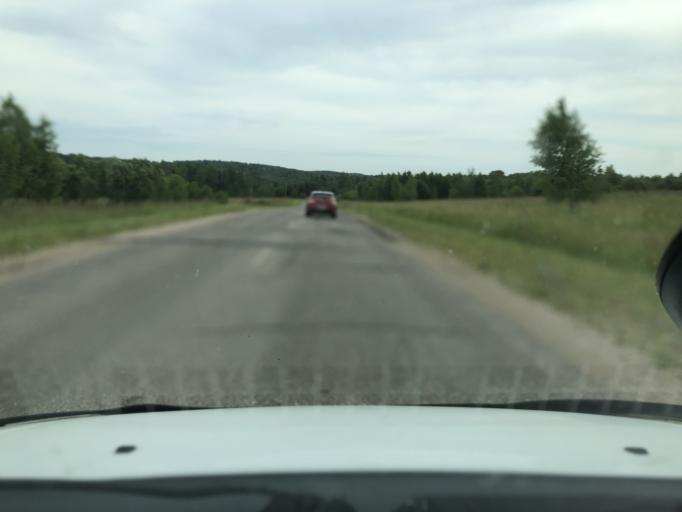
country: RU
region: Jaroslavl
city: Petrovsk
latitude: 56.9853
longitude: 39.1321
